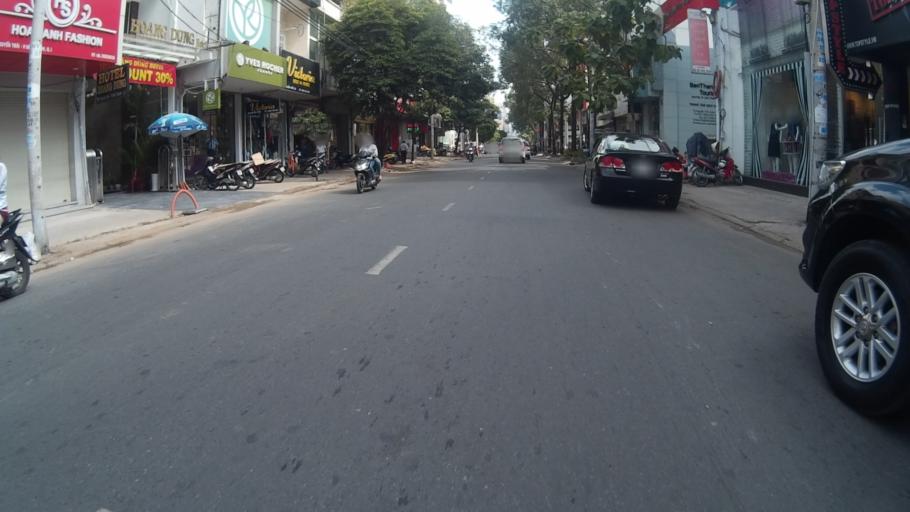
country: VN
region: Ho Chi Minh City
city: Quan Ba
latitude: 10.7697
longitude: 106.6910
